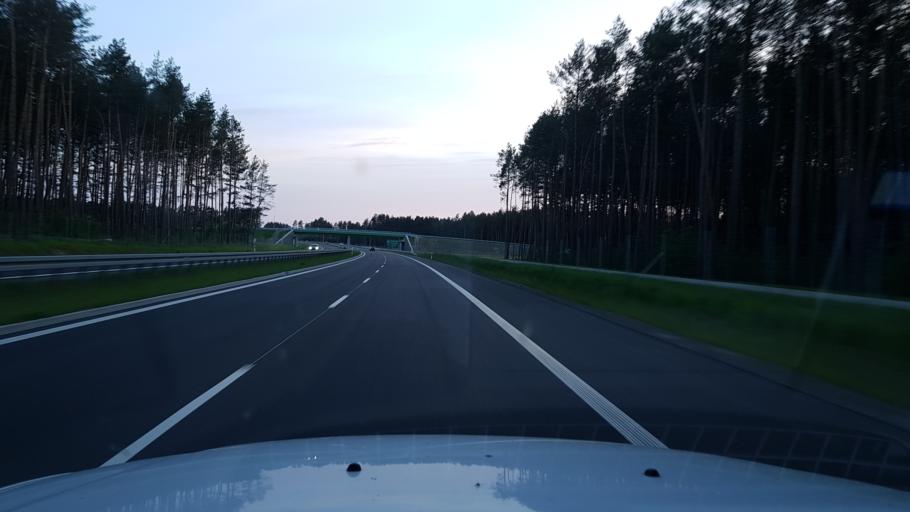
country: PL
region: West Pomeranian Voivodeship
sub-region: Powiat goleniowski
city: Mosty
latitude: 53.6137
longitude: 14.9098
